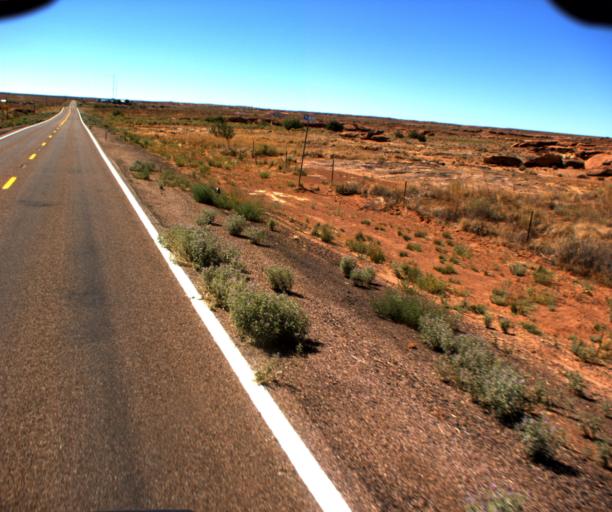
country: US
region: Arizona
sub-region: Navajo County
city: Winslow
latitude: 34.9884
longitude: -110.6654
